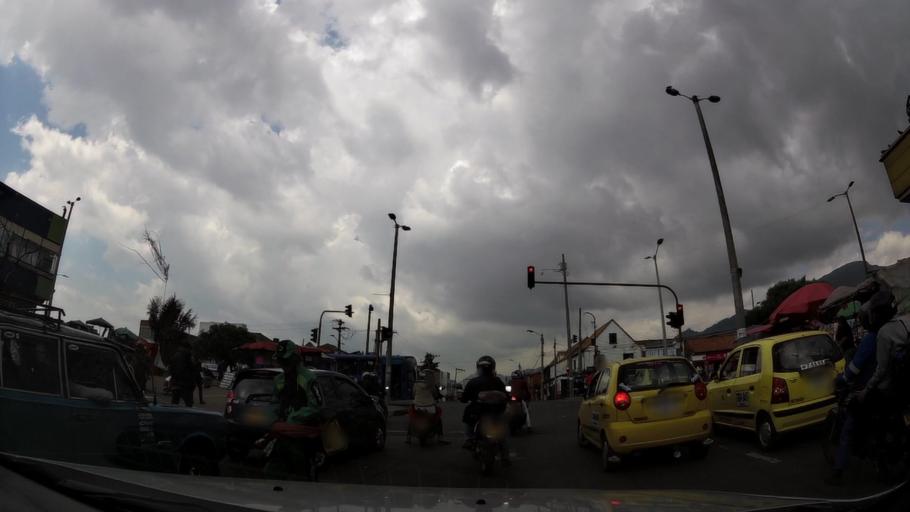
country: CO
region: Bogota D.C.
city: Bogota
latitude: 4.5724
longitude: -74.0917
